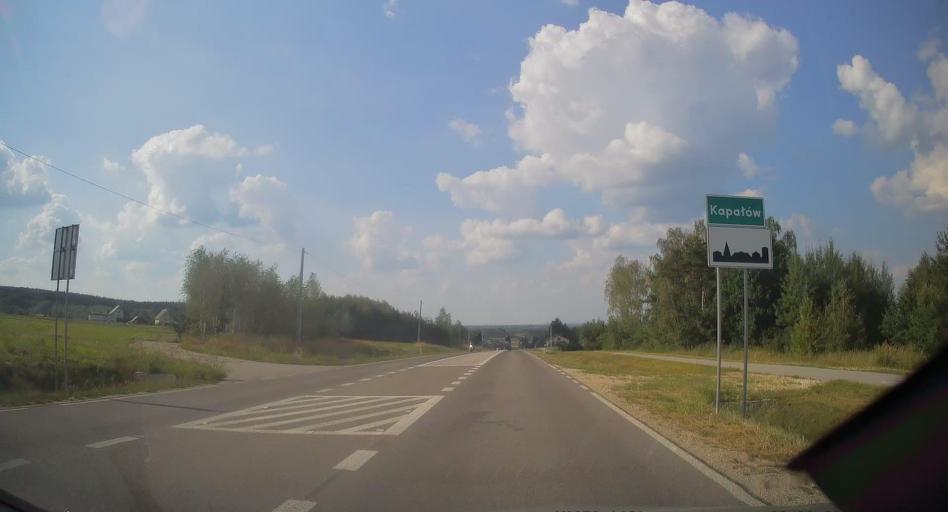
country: PL
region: Swietokrzyskie
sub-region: Powiat konecki
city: Radoszyce
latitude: 51.0358
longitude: 20.2854
